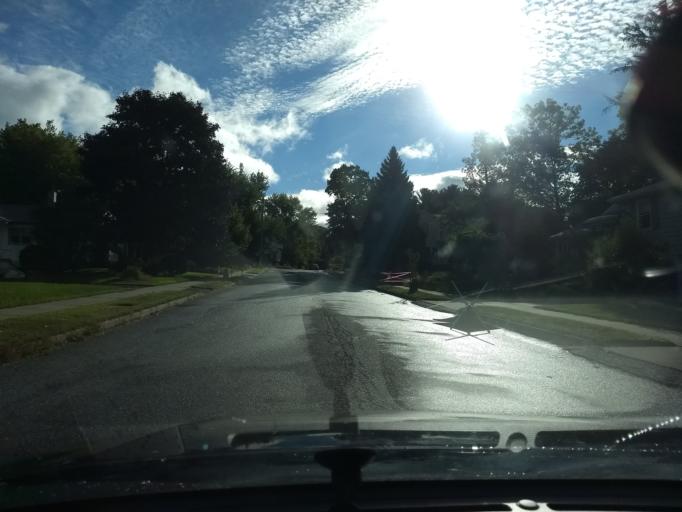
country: US
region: Vermont
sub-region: Chittenden County
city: Burlington
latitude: 44.4586
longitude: -73.2105
